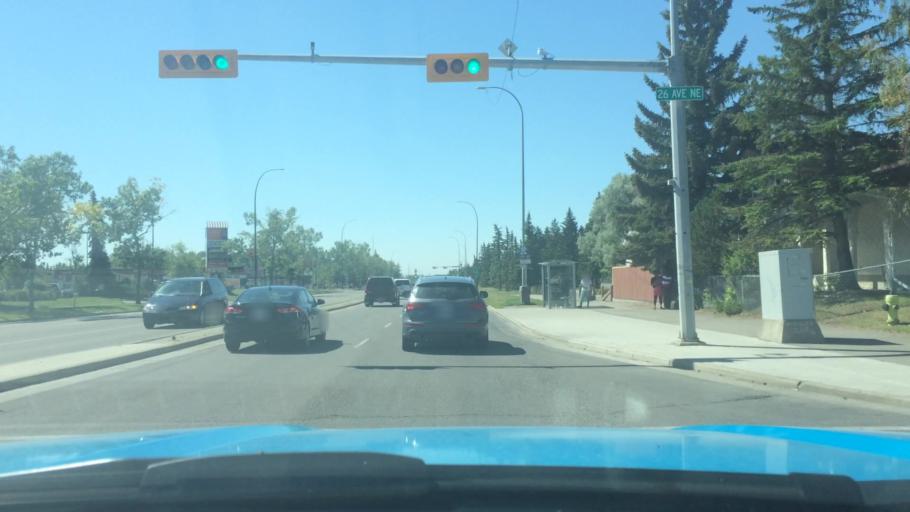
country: CA
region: Alberta
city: Calgary
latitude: 51.0762
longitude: -113.9585
